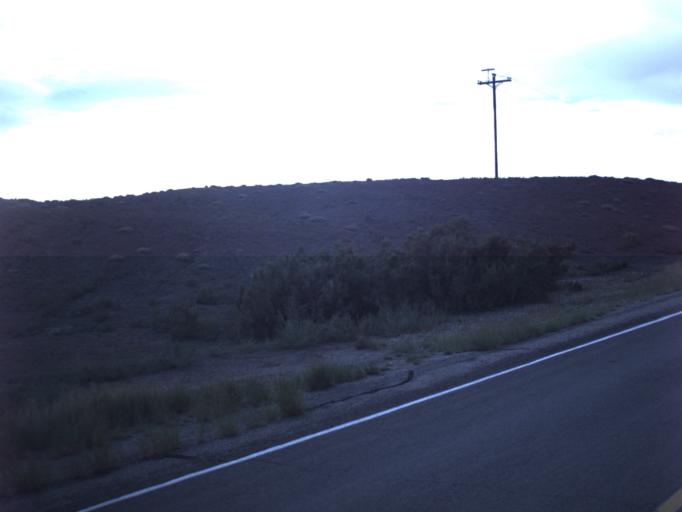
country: US
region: Utah
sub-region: Grand County
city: Moab
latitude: 38.8803
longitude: -109.3106
